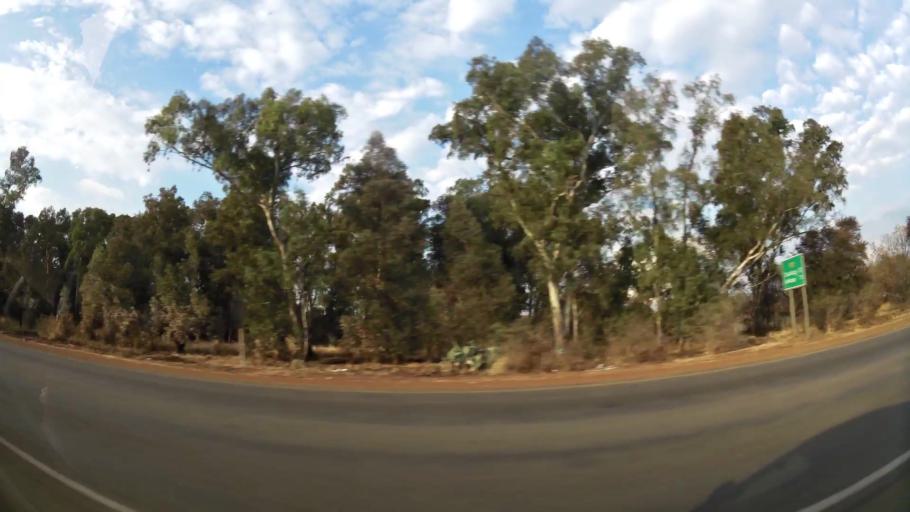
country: ZA
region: Gauteng
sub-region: Sedibeng District Municipality
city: Vanderbijlpark
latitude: -26.7134
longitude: 27.8175
